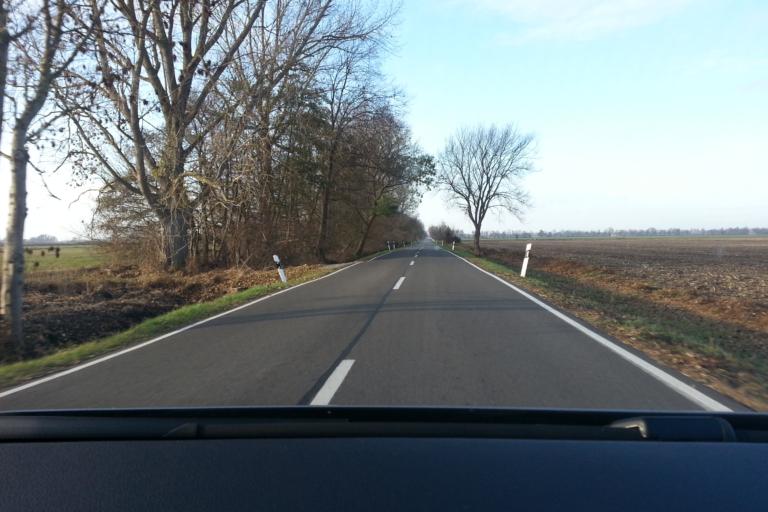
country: DE
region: Mecklenburg-Vorpommern
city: Strasburg
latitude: 53.6289
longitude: 13.7598
